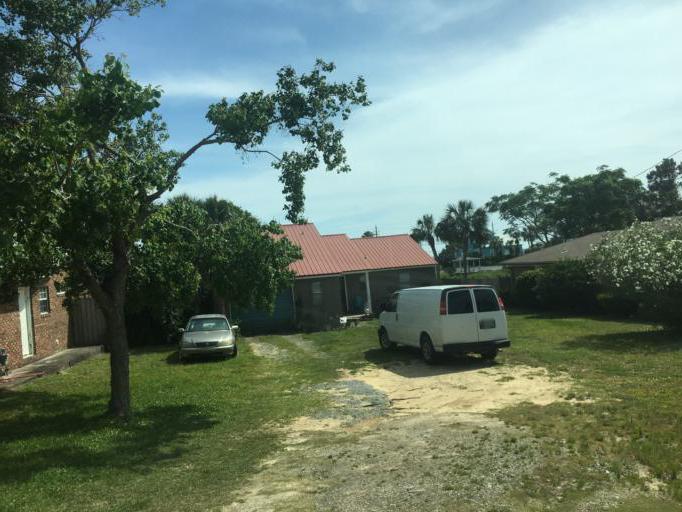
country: US
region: Florida
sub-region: Bay County
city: Laguna Beach
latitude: 30.2491
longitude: -85.9411
